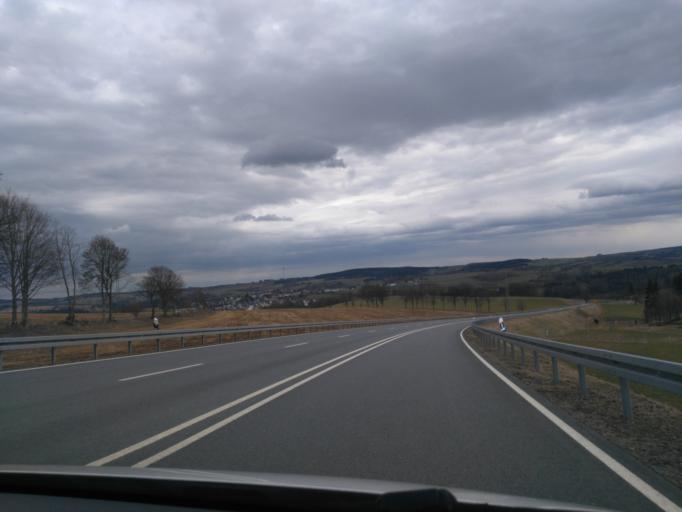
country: DE
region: Saxony
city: Drebach
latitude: 50.6480
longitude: 13.0373
